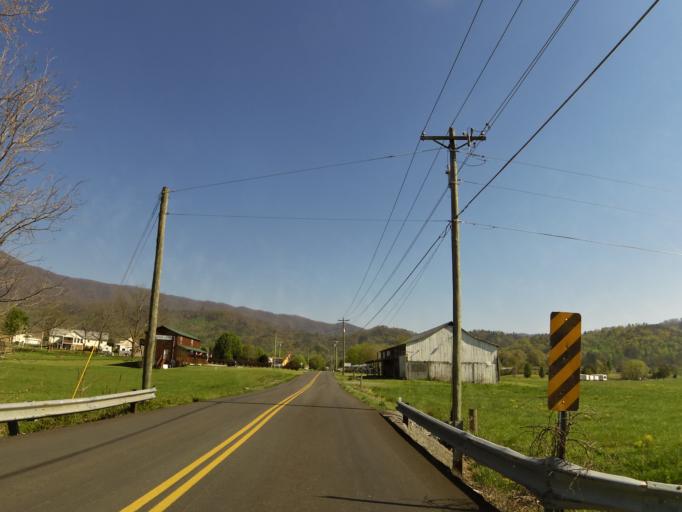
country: US
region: Tennessee
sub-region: Sevier County
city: Pigeon Forge
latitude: 35.7114
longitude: -83.6514
